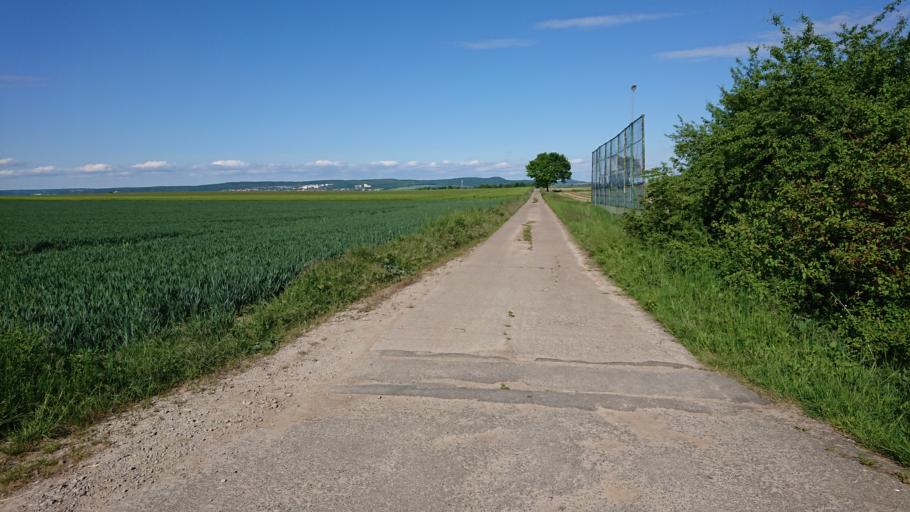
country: DE
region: Lower Saxony
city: Rosdorf
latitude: 51.4758
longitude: 9.8913
